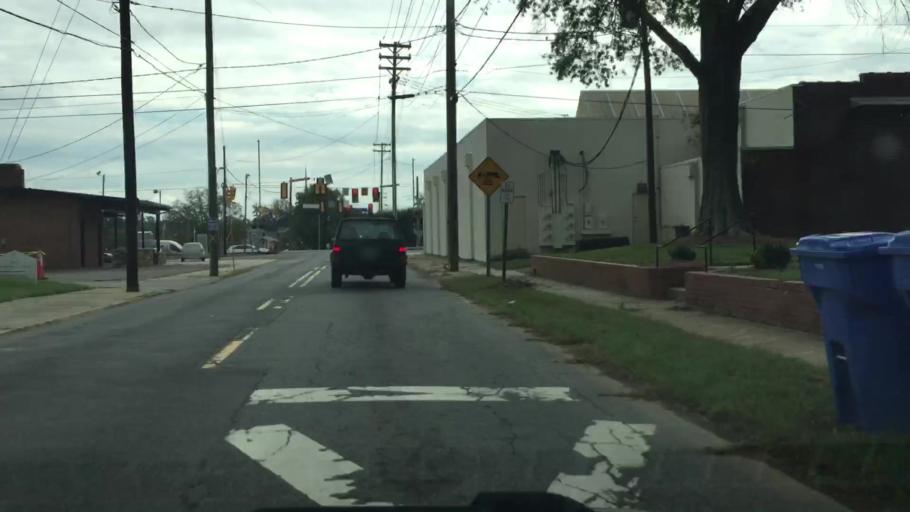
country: US
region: North Carolina
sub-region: Iredell County
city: Mooresville
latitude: 35.5825
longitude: -80.8147
